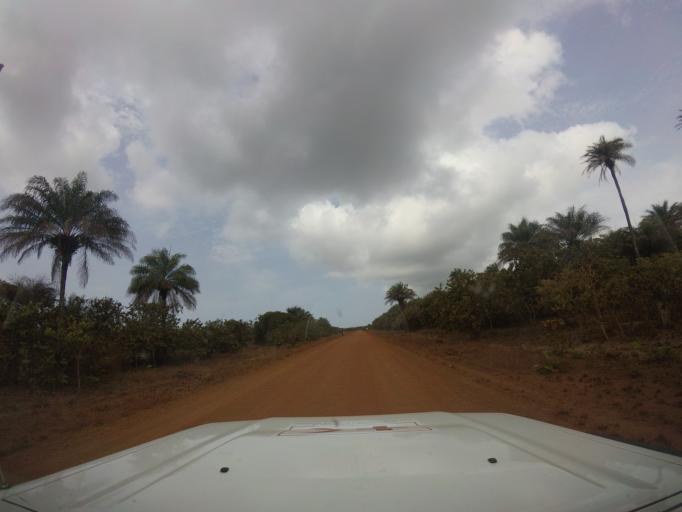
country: LR
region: Grand Cape Mount
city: Robertsport
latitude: 6.6916
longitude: -11.2713
